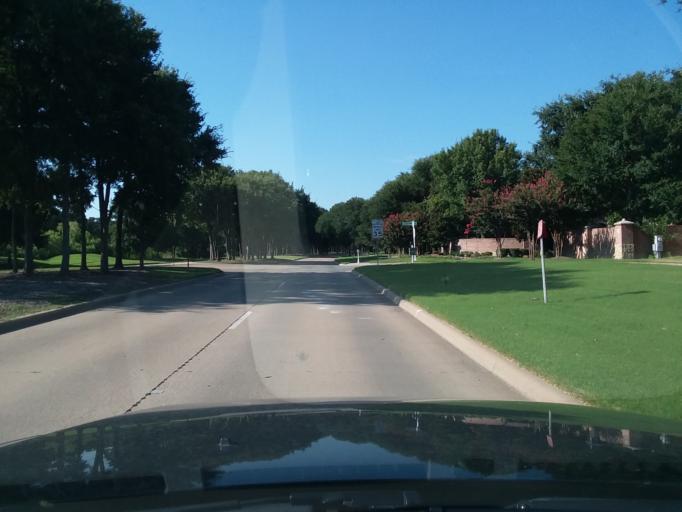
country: US
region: Texas
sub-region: Denton County
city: Double Oak
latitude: 33.0483
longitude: -97.0934
